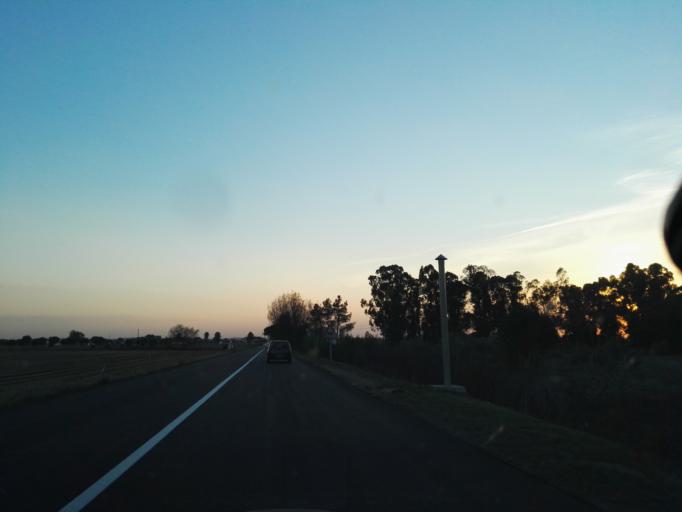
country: PT
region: Santarem
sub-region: Coruche
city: Coruche
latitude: 38.9623
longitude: -8.4861
